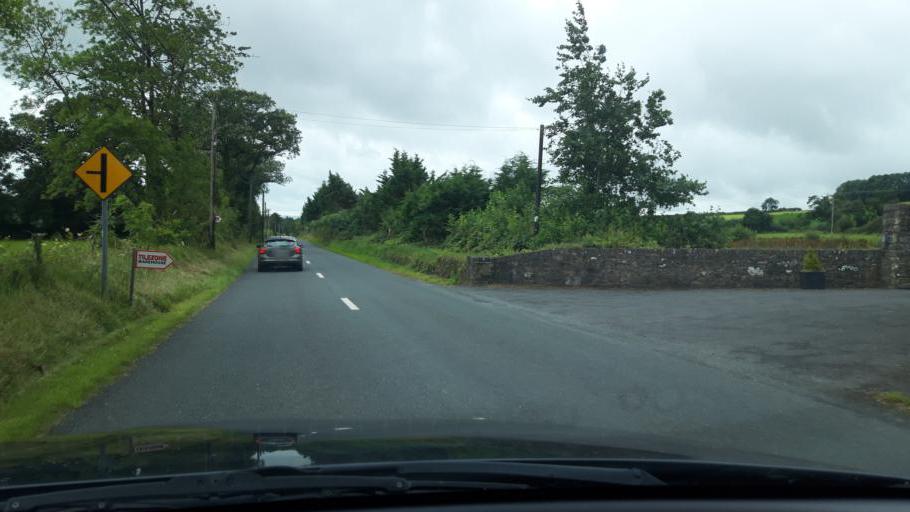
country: IE
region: Munster
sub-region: County Cork
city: Youghal
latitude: 52.1582
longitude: -7.8417
